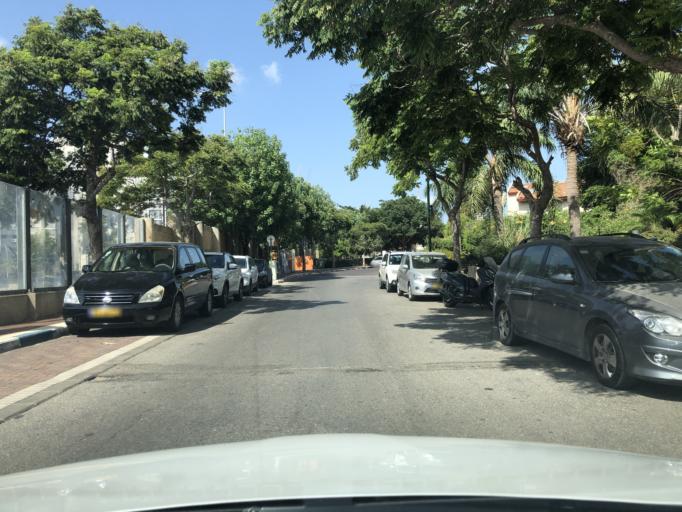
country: IL
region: Tel Aviv
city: Giv`at Shemu'el
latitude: 32.0653
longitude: 34.8458
